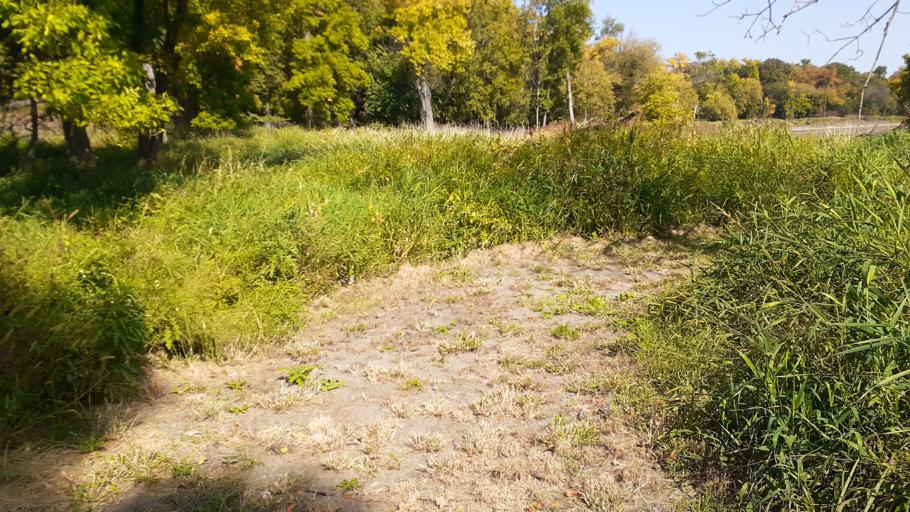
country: US
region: Minnesota
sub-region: Clay County
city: Oakport
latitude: 46.9117
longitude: -96.7645
